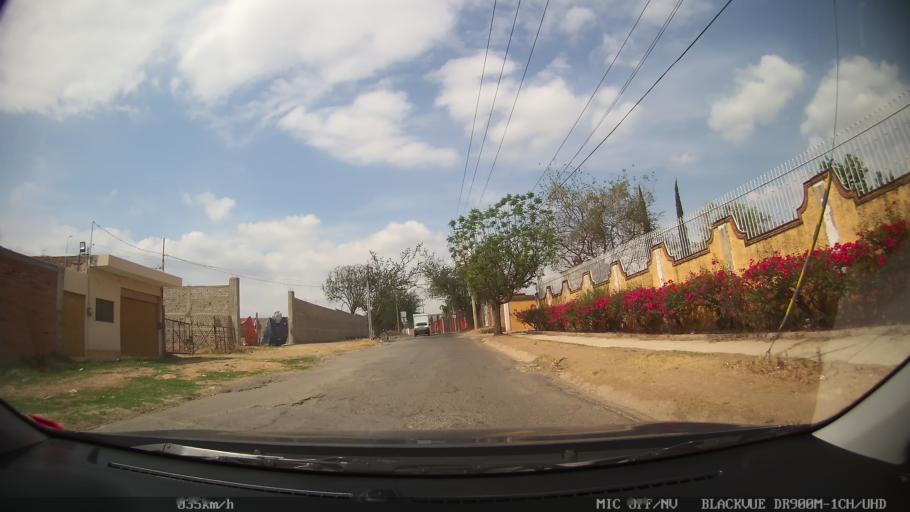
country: MX
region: Jalisco
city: Tonala
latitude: 20.6439
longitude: -103.2228
